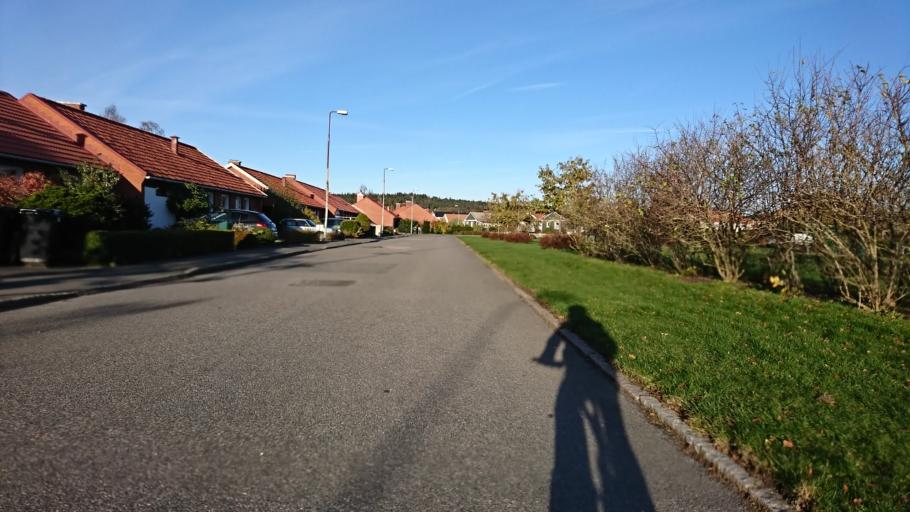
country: SE
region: Vaestra Goetaland
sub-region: Molndal
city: Moelndal
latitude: 57.6535
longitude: 11.9910
